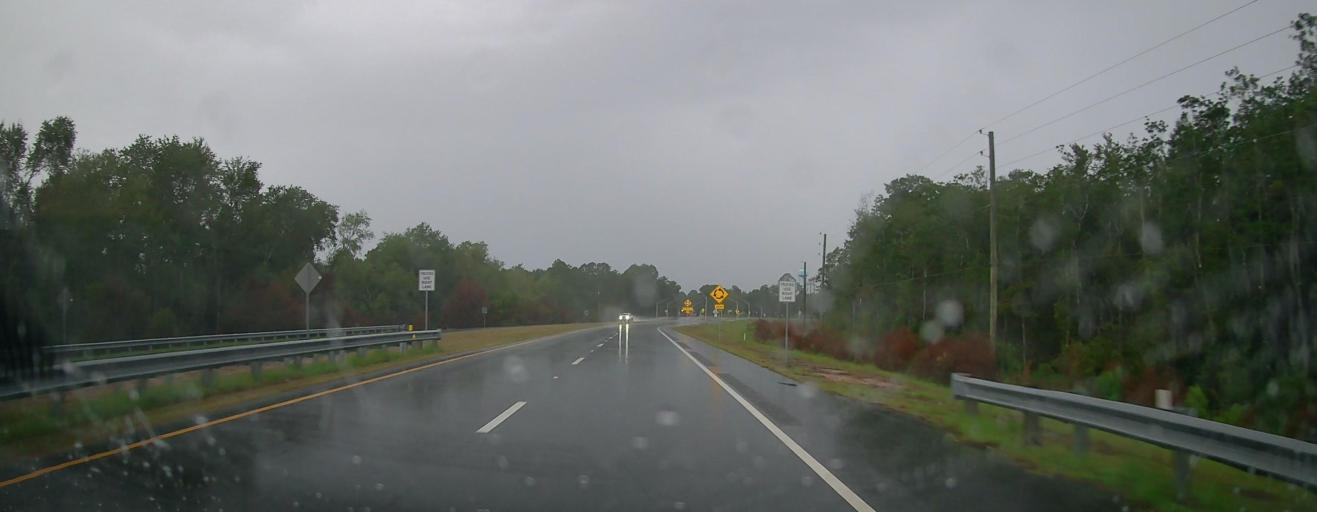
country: US
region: Georgia
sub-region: Clinch County
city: Homerville
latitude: 31.0772
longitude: -82.6423
